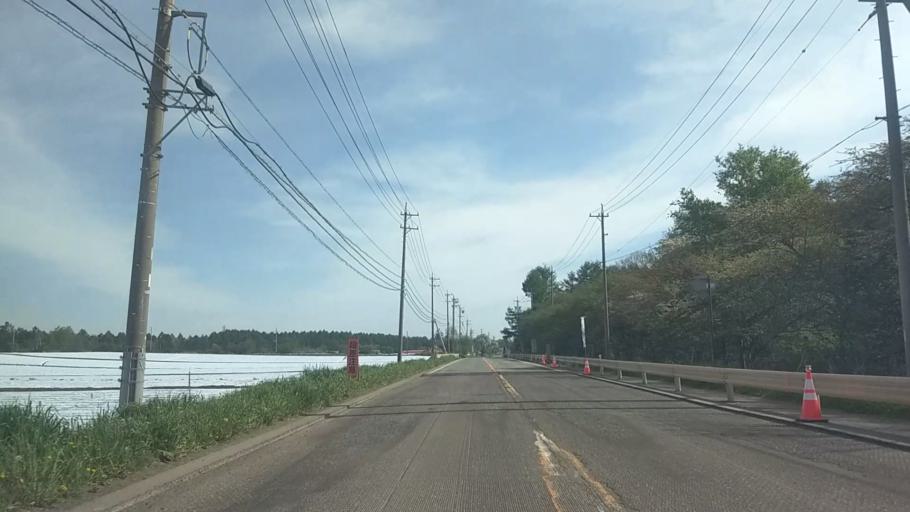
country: JP
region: Nagano
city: Saku
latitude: 35.9654
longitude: 138.4767
